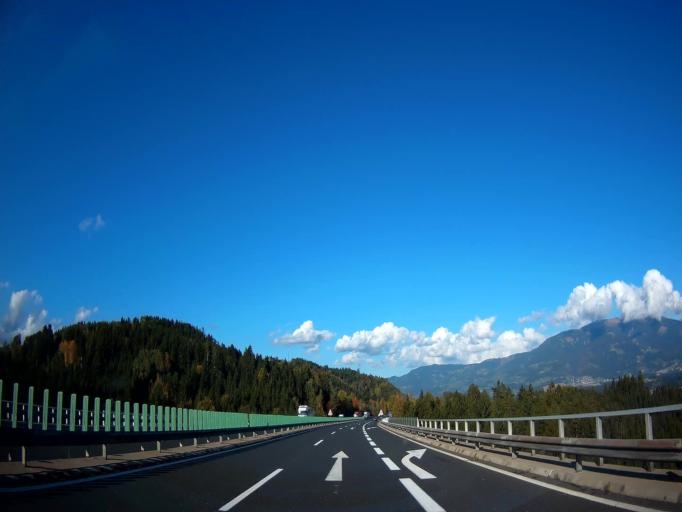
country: AT
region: Carinthia
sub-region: Politischer Bezirk Wolfsberg
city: Sankt Andrae
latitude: 46.7417
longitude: 14.8058
